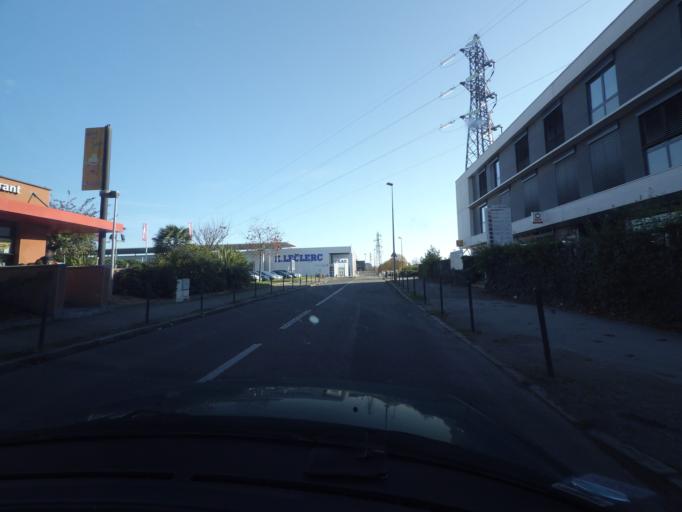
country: FR
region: Pays de la Loire
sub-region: Departement de la Loire-Atlantique
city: Sainte-Luce-sur-Loire
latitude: 47.2498
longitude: -1.5185
